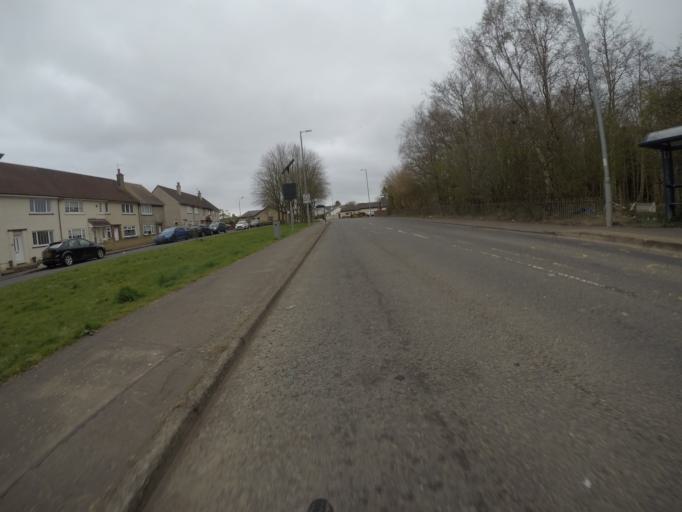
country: GB
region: Scotland
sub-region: North Ayrshire
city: Springside
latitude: 55.6136
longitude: -4.5851
